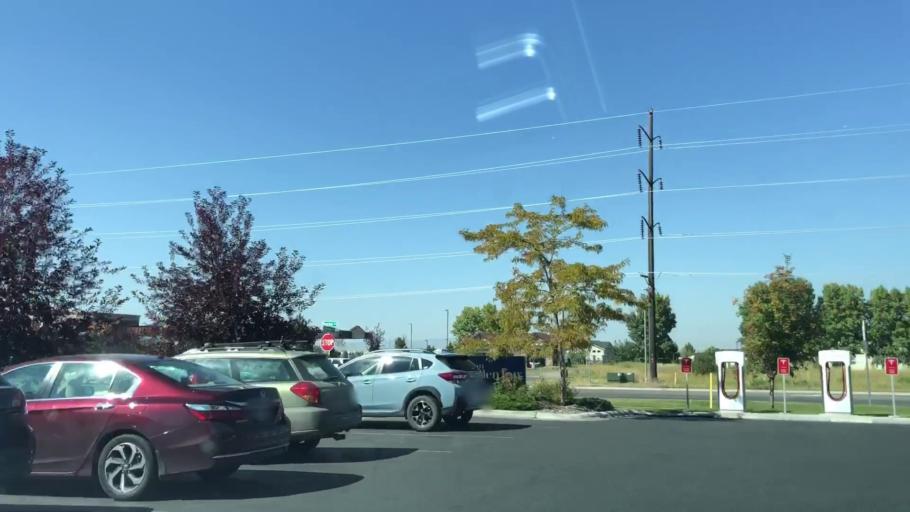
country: US
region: Montana
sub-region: Gallatin County
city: Bozeman
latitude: 45.6998
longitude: -111.0632
